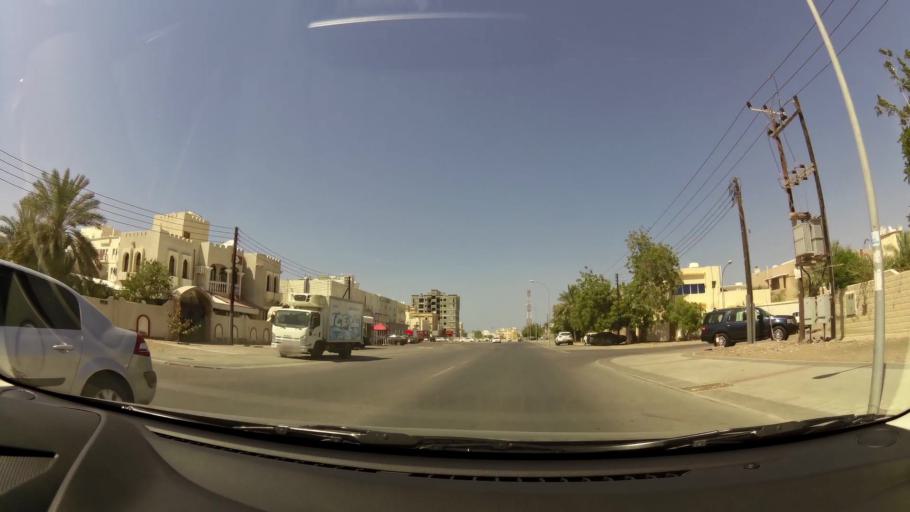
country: OM
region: Muhafazat Masqat
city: As Sib al Jadidah
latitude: 23.6236
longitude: 58.2196
